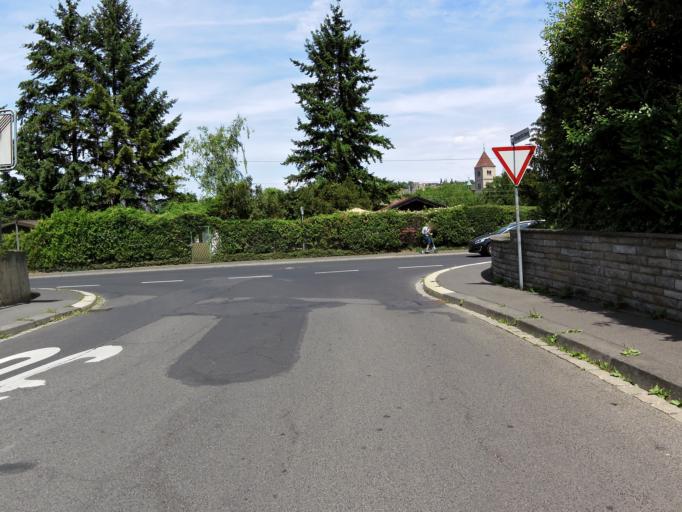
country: DE
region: Bavaria
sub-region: Regierungsbezirk Unterfranken
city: Randersacker
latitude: 49.7610
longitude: 9.9500
